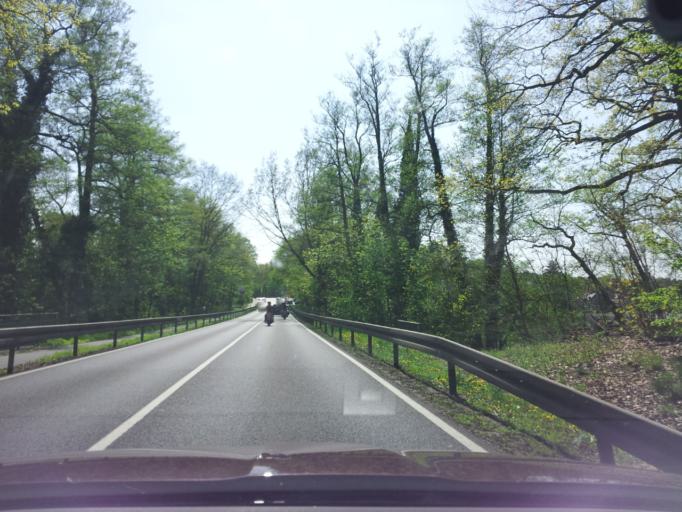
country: DE
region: Brandenburg
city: Michendorf
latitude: 52.2761
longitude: 13.0049
